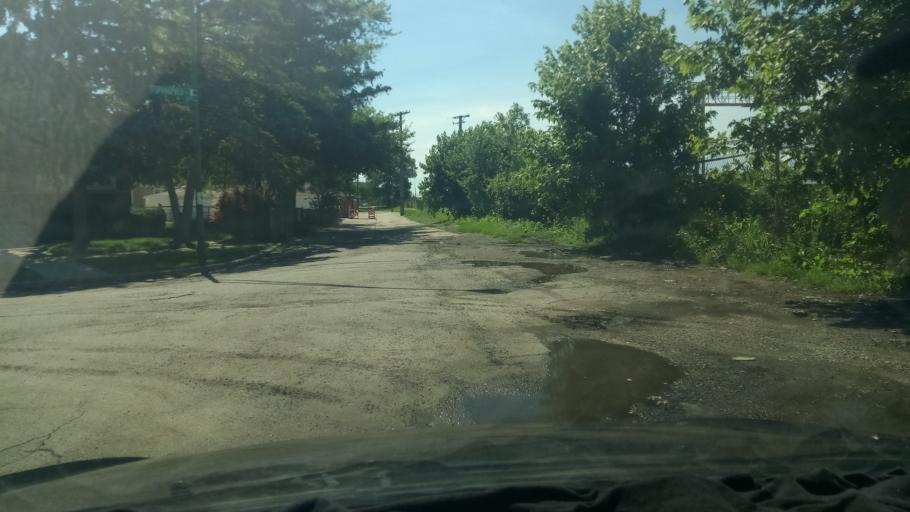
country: US
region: Illinois
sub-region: Cook County
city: Hometown
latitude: 41.7615
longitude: -87.7201
